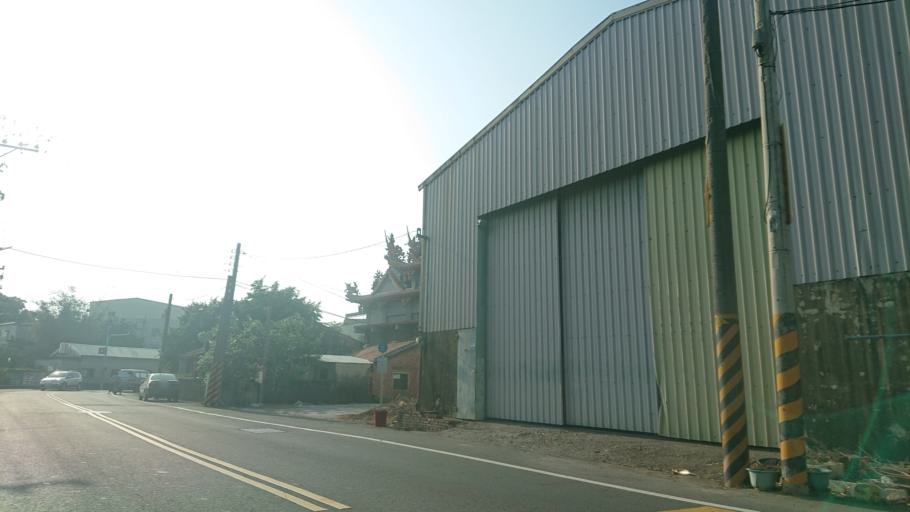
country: TW
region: Taiwan
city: Xinying
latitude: 23.1767
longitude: 120.2598
